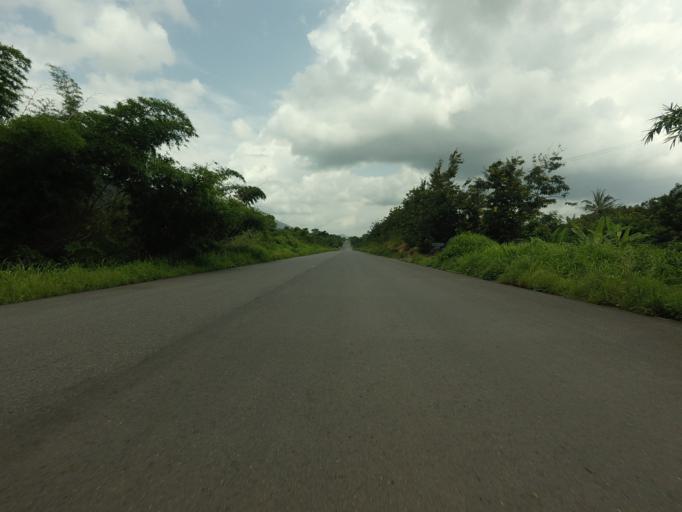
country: GH
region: Volta
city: Ho
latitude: 6.6148
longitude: 0.3029
